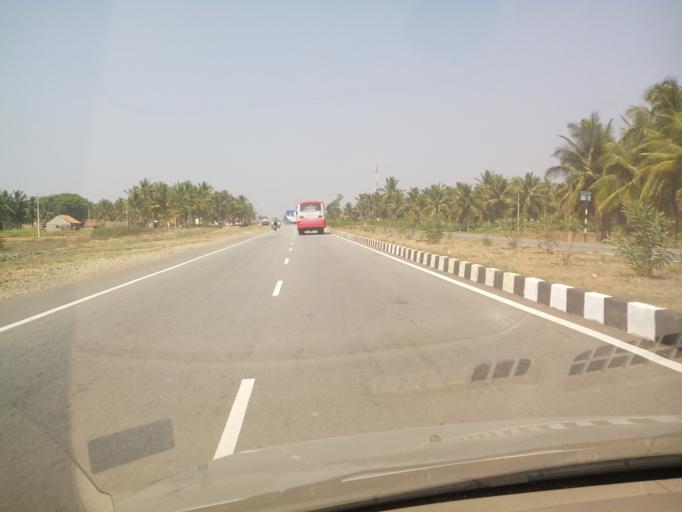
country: IN
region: Karnataka
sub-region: Hassan
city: Channarayapatna
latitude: 12.9081
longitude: 76.4310
